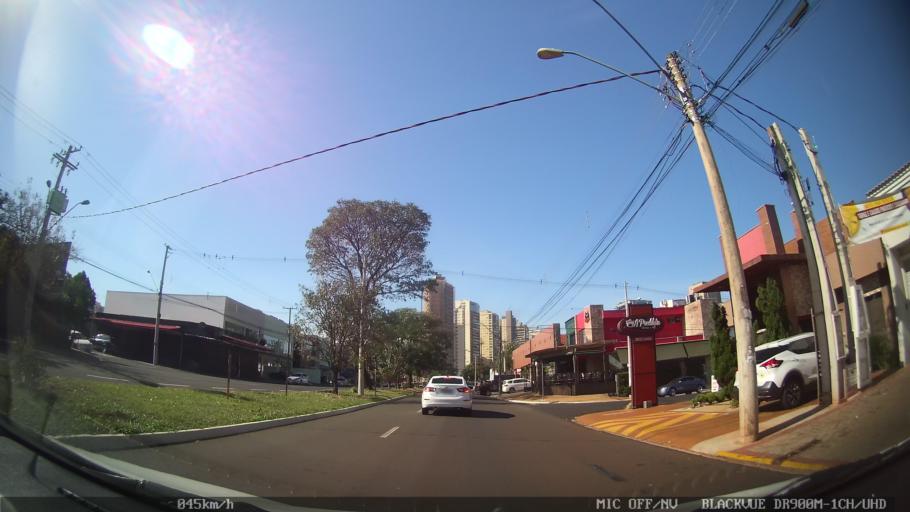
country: BR
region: Sao Paulo
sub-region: Ribeirao Preto
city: Ribeirao Preto
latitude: -21.2025
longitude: -47.8119
